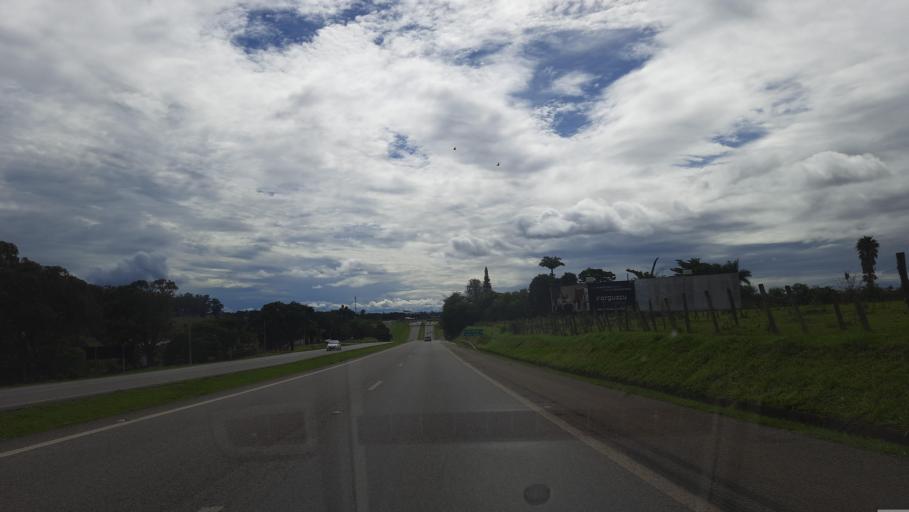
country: BR
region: Sao Paulo
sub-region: Sao Joao Da Boa Vista
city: Sao Joao da Boa Vista
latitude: -21.9734
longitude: -46.7495
